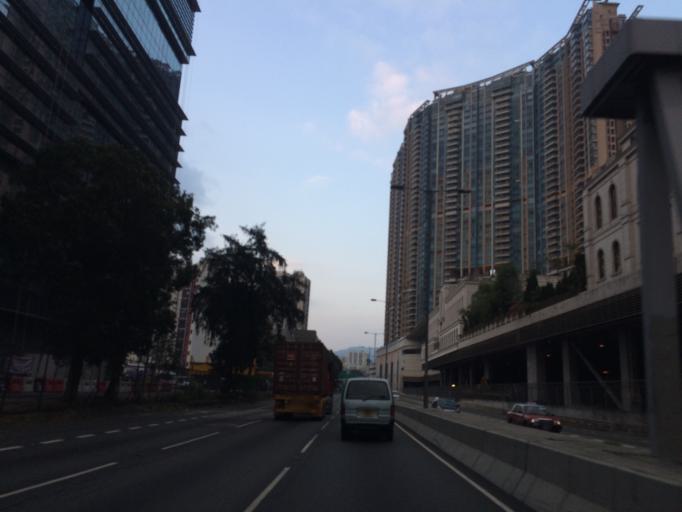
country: HK
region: Sha Tin
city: Sha Tin
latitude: 22.3974
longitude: 114.2012
